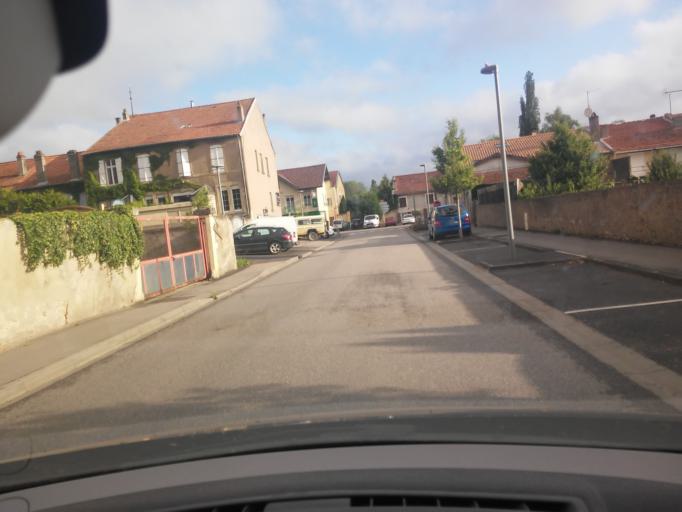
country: FR
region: Lorraine
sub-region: Departement de Meurthe-et-Moselle
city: Jarny
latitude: 49.0981
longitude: 5.8880
